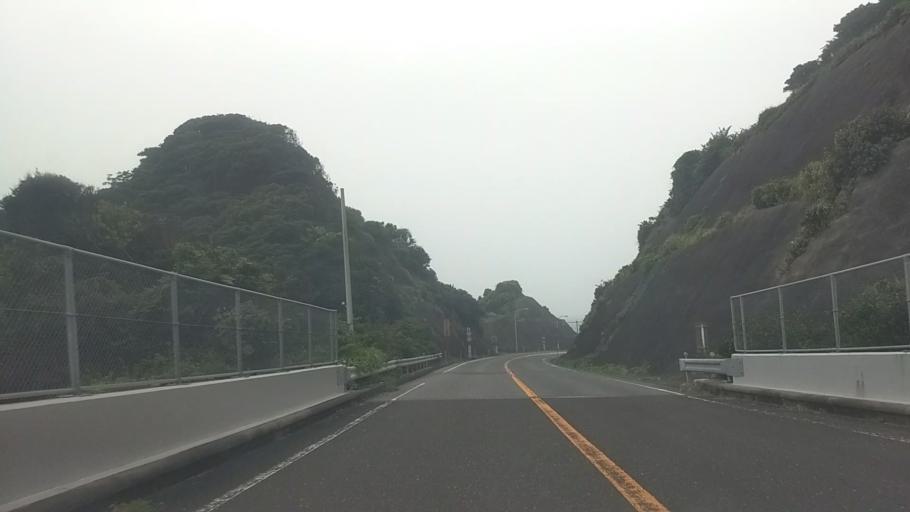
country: JP
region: Chiba
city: Katsuura
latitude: 35.1539
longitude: 140.3056
